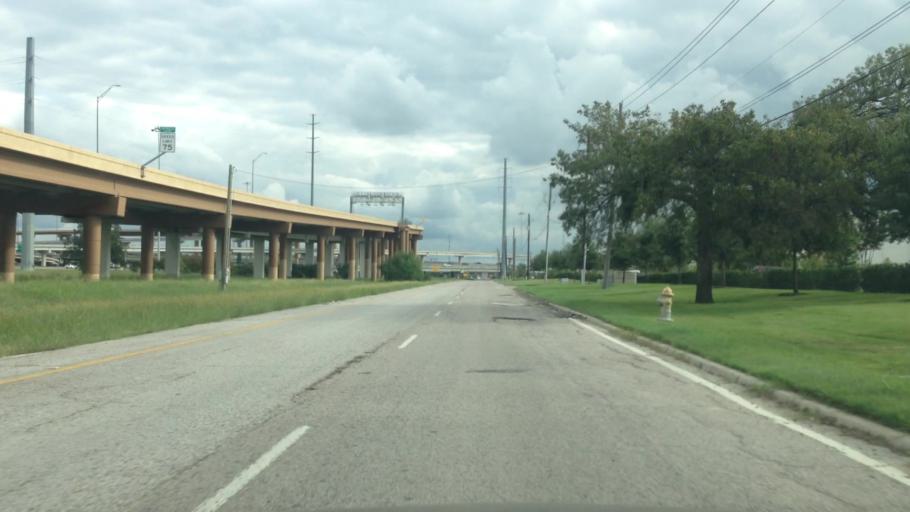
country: US
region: Texas
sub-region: Dallas County
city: Farmers Branch
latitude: 32.9130
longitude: -96.8999
